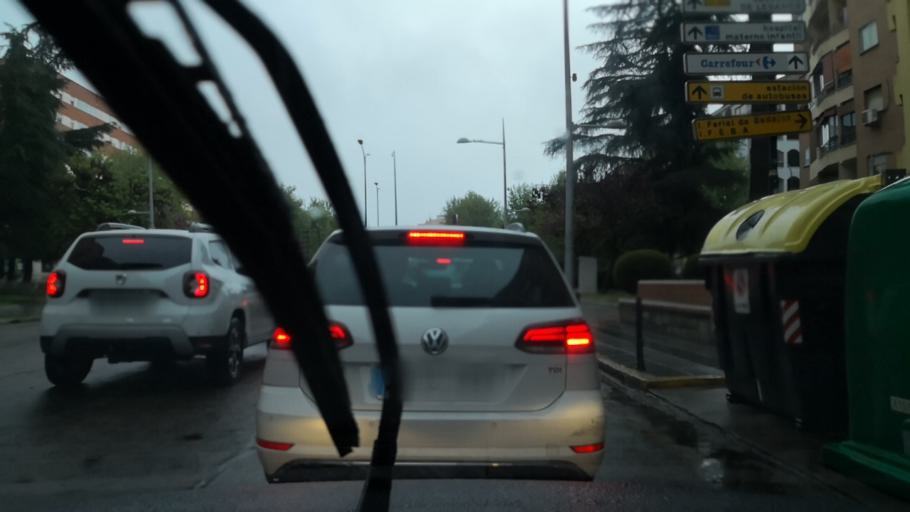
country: ES
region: Extremadura
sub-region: Provincia de Badajoz
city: Badajoz
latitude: 38.8698
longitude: -6.9731
